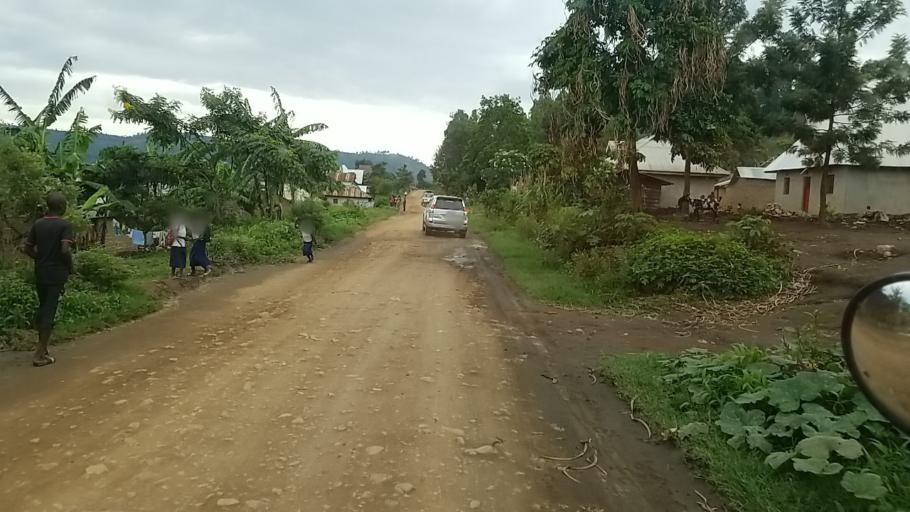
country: CD
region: Nord Kivu
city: Sake
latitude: -1.6710
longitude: 29.0171
